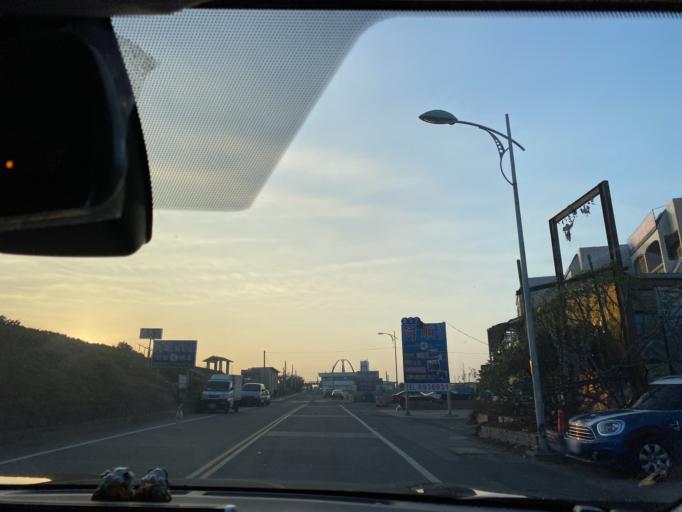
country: TW
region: Taiwan
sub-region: Changhua
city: Chang-hua
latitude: 23.9680
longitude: 120.3278
